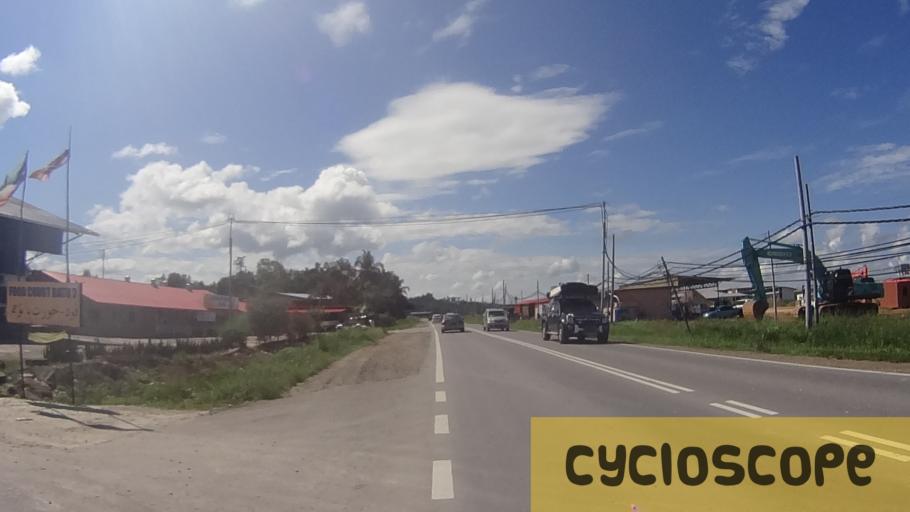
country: MY
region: Sabah
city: Beaufort
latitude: 5.3393
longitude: 115.7225
